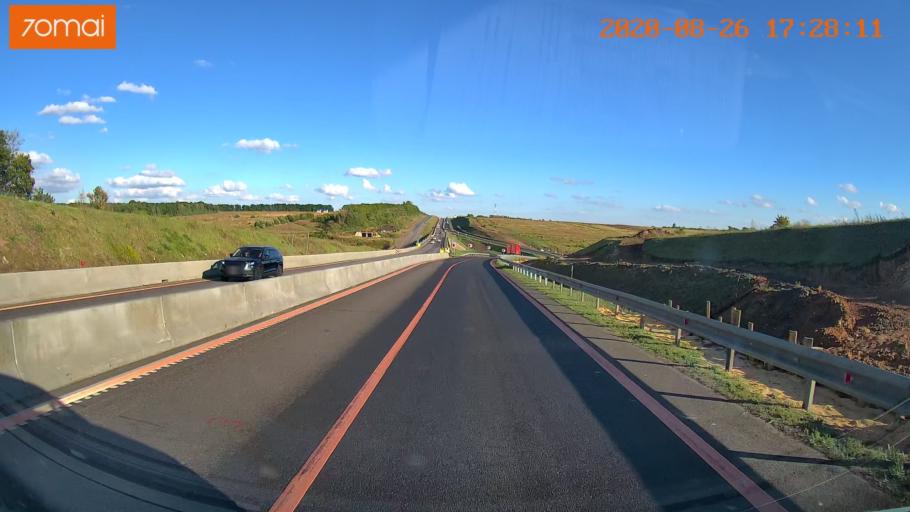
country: RU
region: Tula
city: Kazachka
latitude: 53.4650
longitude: 38.1313
